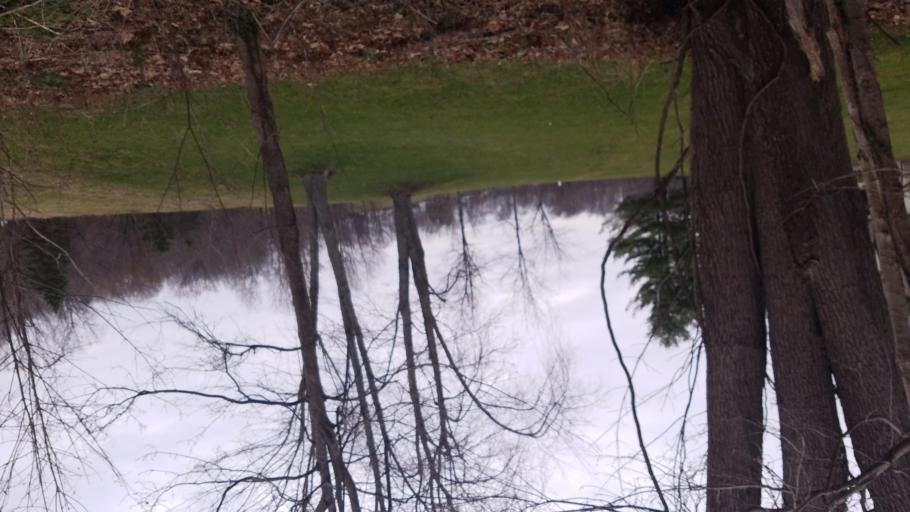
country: US
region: Ohio
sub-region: Sandusky County
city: Bellville
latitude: 40.6836
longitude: -82.4950
